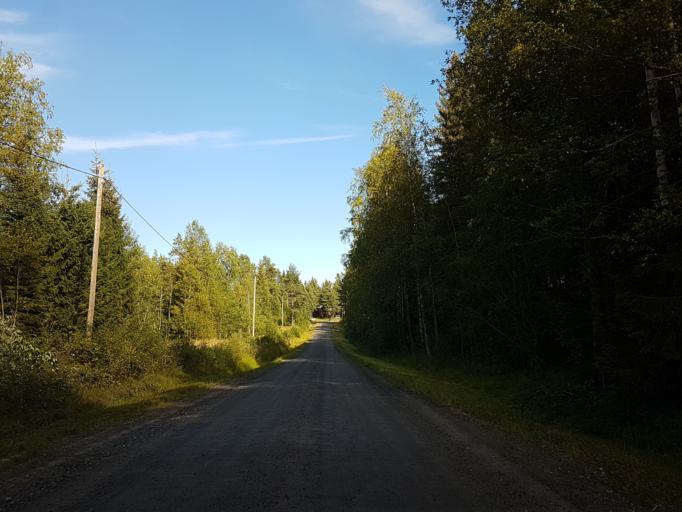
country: SE
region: Vaesterbotten
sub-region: Robertsfors Kommun
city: Robertsfors
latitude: 64.0492
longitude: 20.8795
